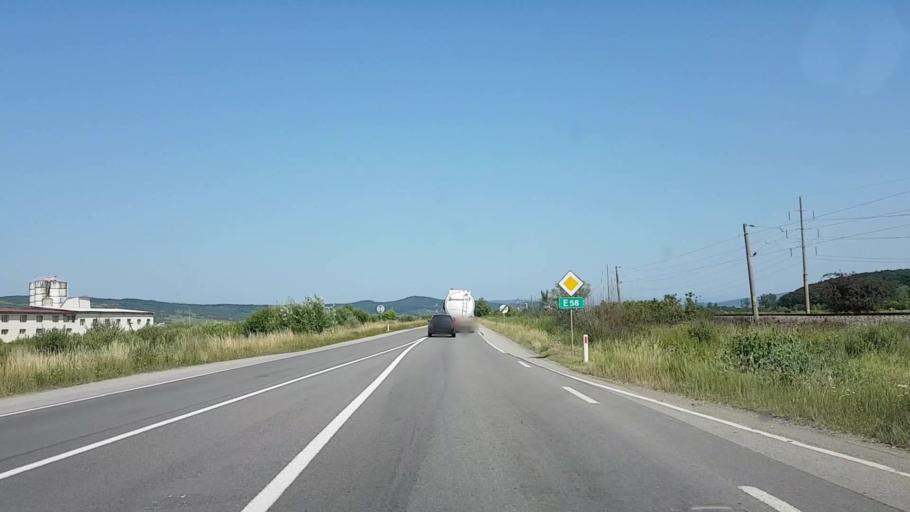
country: RO
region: Bistrita-Nasaud
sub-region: Comuna Sintereag
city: Cociu
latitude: 47.1825
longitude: 24.2406
